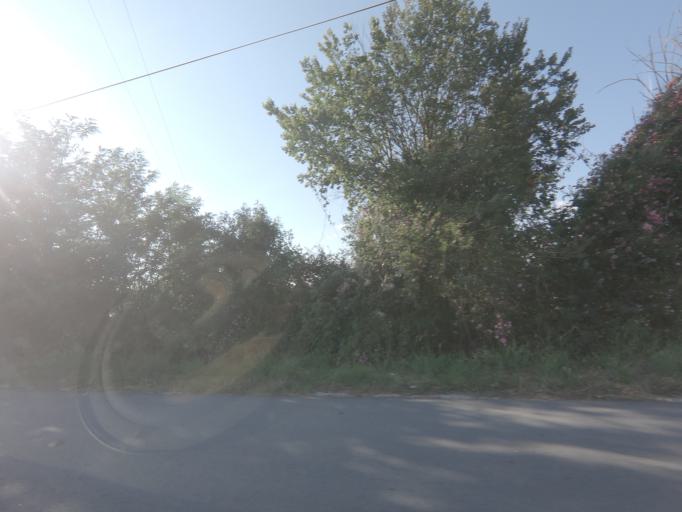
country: PT
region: Vila Real
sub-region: Chaves
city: Chaves
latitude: 41.7921
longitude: -7.4308
